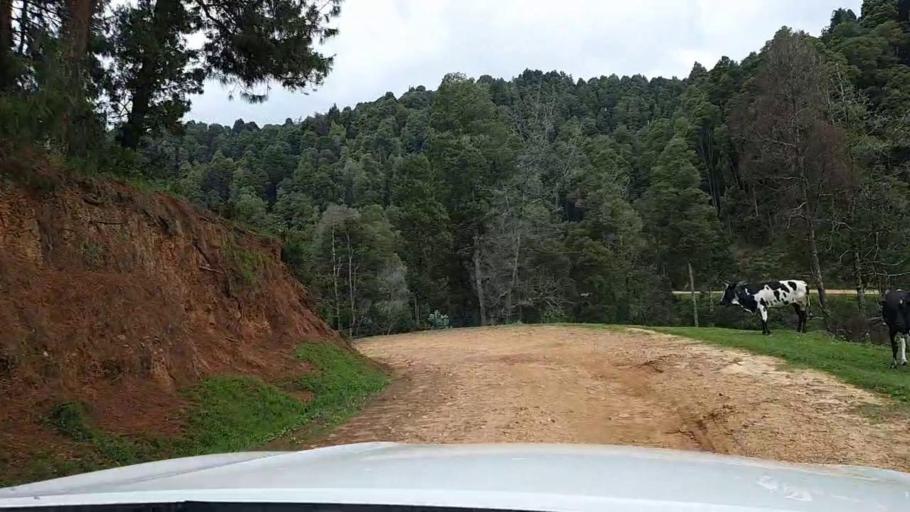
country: RW
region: Western Province
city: Kibuye
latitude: -2.2903
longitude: 29.3698
